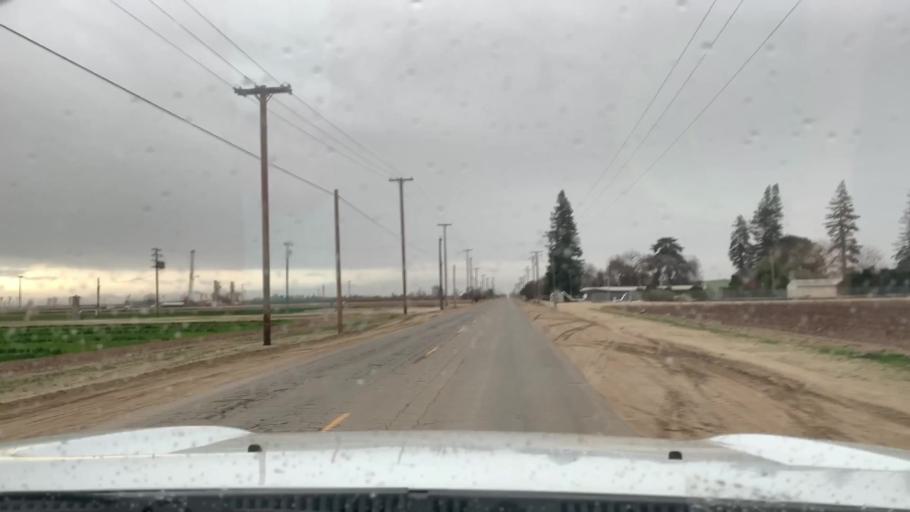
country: US
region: California
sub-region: Kern County
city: Shafter
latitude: 35.5345
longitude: -119.2778
